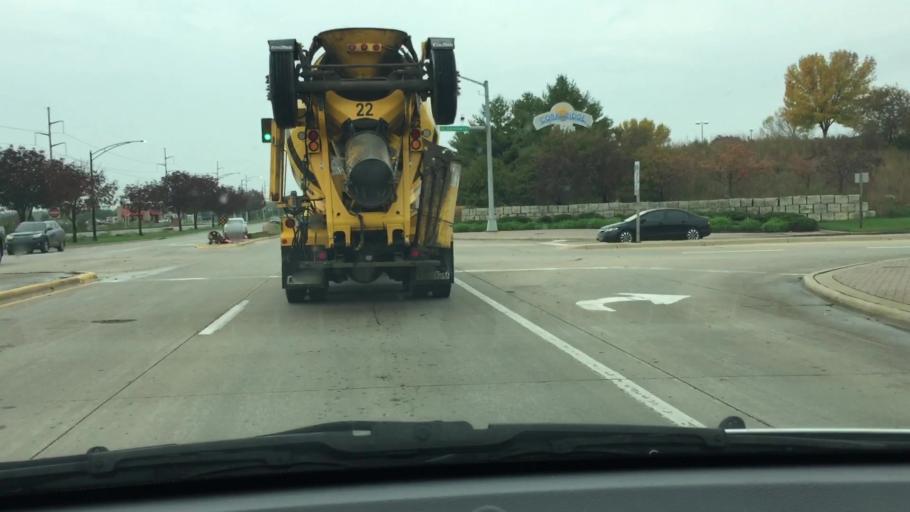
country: US
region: Iowa
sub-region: Johnson County
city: Coralville
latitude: 41.6871
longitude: -91.6061
